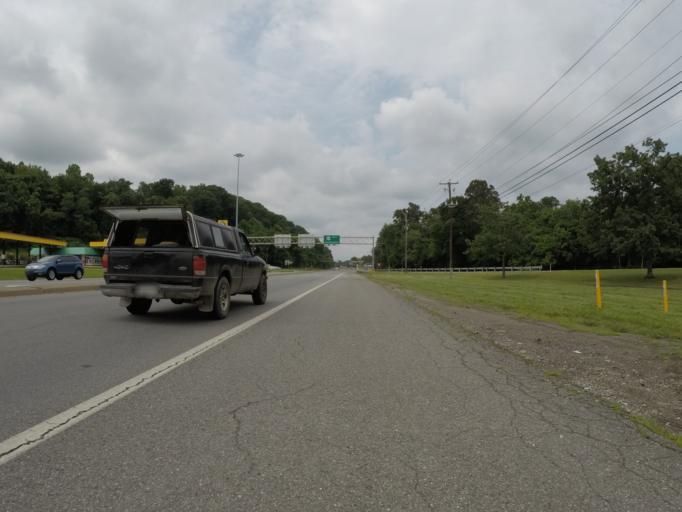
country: US
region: West Virginia
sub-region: Cabell County
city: Pea Ridge
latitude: 38.4134
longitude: -82.3504
